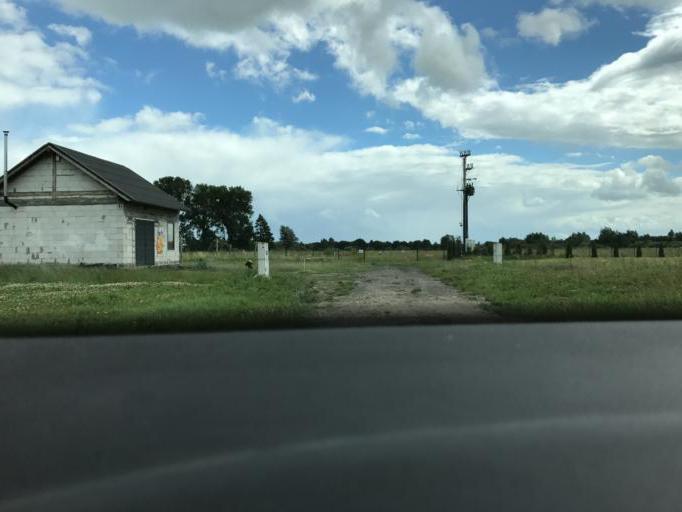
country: PL
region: Pomeranian Voivodeship
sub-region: Powiat gdanski
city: Pruszcz Gdanski
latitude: 54.2713
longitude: 18.6842
